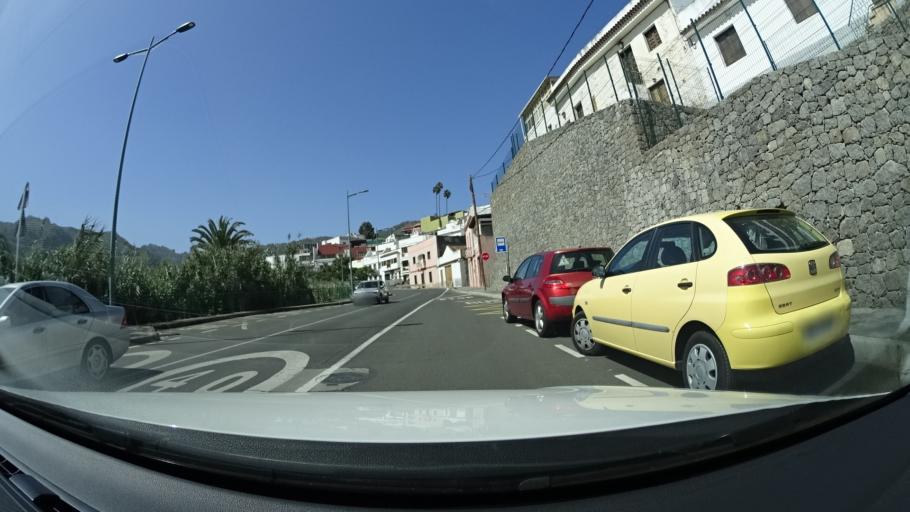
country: ES
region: Canary Islands
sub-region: Provincia de Las Palmas
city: Teror
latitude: 28.0620
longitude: -15.5429
